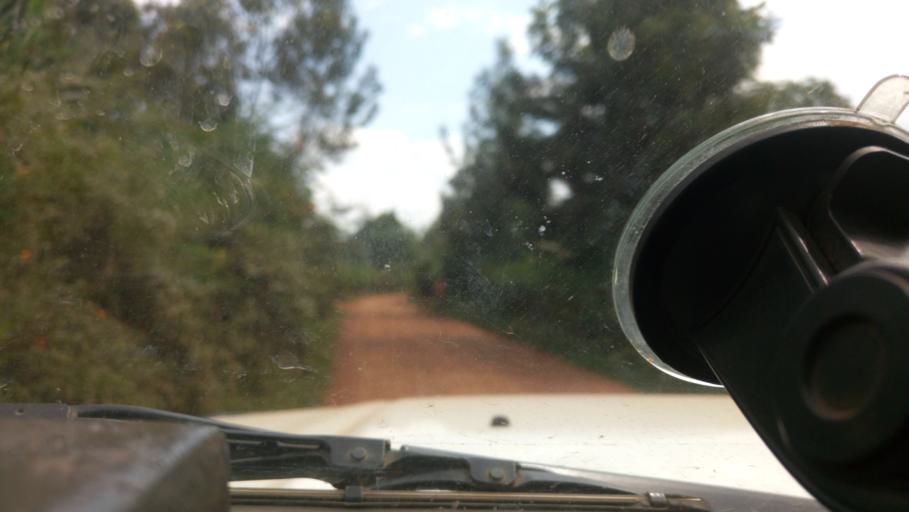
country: KE
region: Kericho
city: Litein
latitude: -0.5744
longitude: 35.1694
